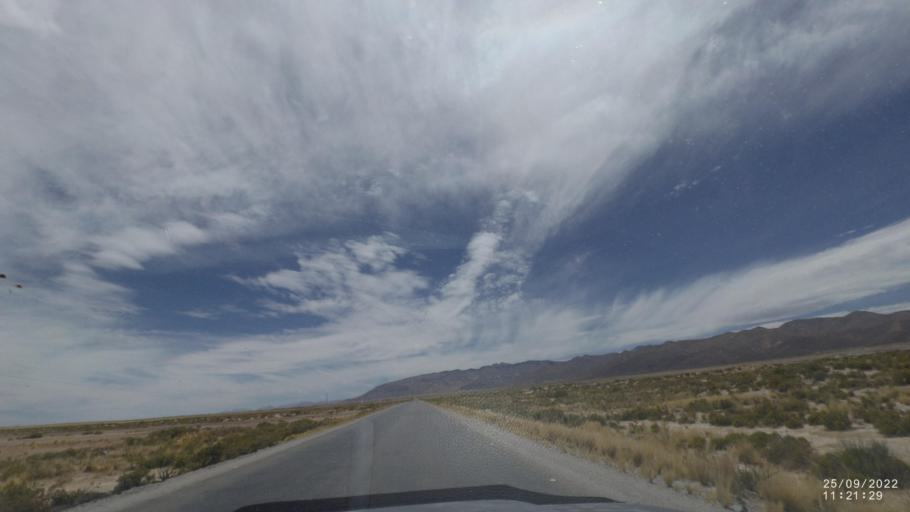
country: BO
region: Oruro
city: Challapata
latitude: -19.1427
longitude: -66.7705
